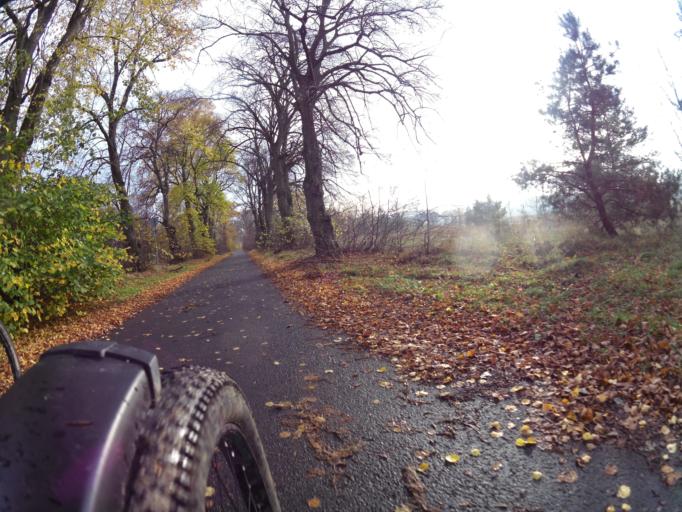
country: PL
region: Pomeranian Voivodeship
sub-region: Powiat wejherowski
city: Gniewino
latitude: 54.7130
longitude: 18.0951
